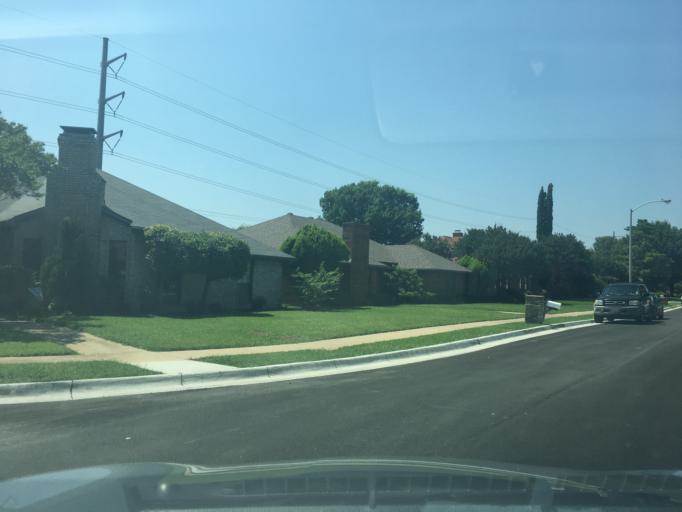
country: US
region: Texas
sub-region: Dallas County
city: Richardson
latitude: 32.9276
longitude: -96.7116
